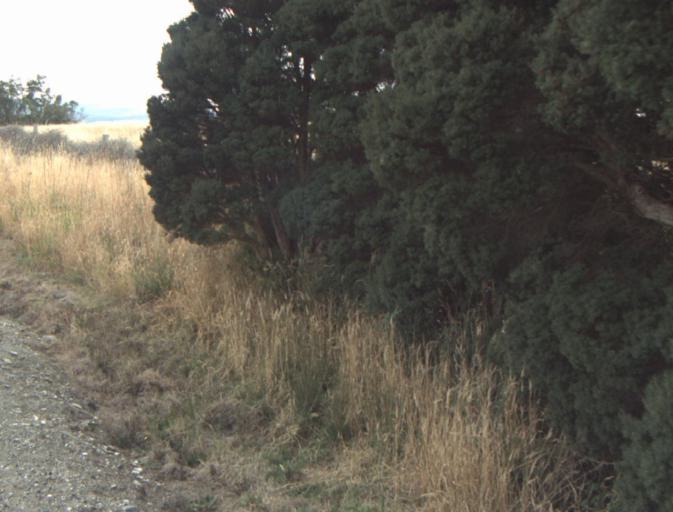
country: AU
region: Tasmania
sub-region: Launceston
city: Mayfield
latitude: -41.2172
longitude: 147.1069
